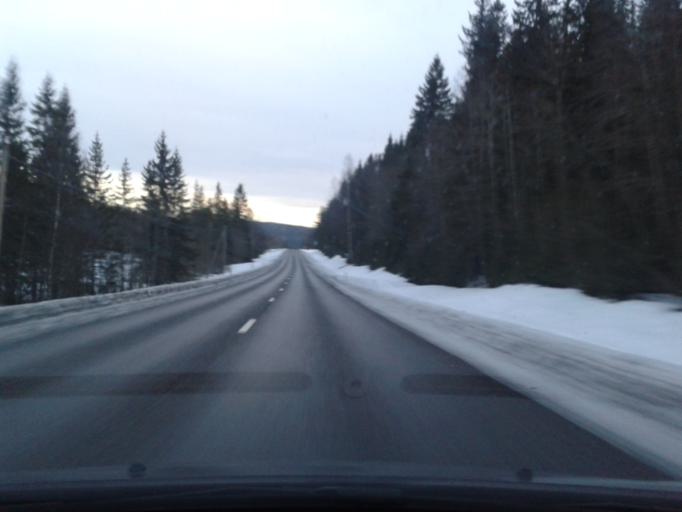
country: SE
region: Vaesternorrland
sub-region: Kramfors Kommun
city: Bollstabruk
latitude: 63.0886
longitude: 17.5310
